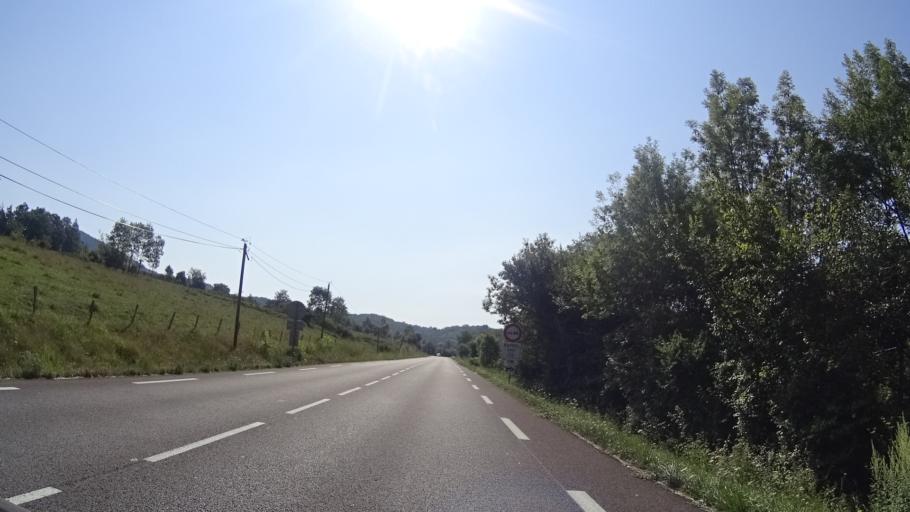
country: FR
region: Midi-Pyrenees
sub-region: Departement de l'Ariege
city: Saint-Paul-de-Jarrat
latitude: 42.9254
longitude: 1.7460
